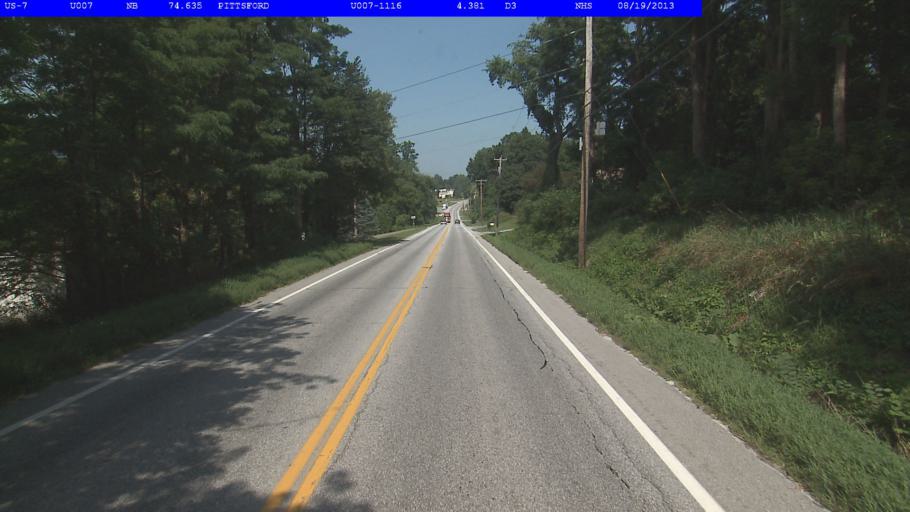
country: US
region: Vermont
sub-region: Rutland County
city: Brandon
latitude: 43.7110
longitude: -73.0334
